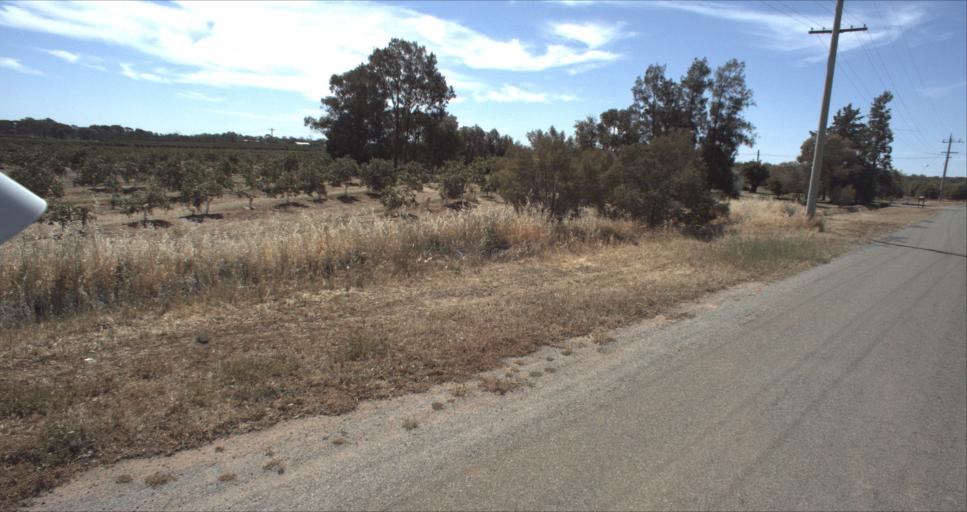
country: AU
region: New South Wales
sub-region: Leeton
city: Leeton
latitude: -34.5972
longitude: 146.4374
